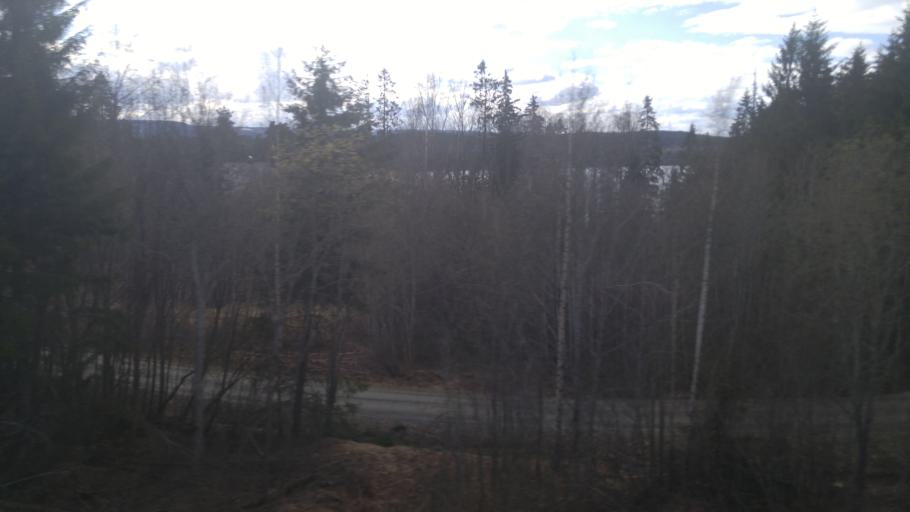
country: NO
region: Hedmark
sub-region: Stange
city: Stange
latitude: 60.6009
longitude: 11.2936
